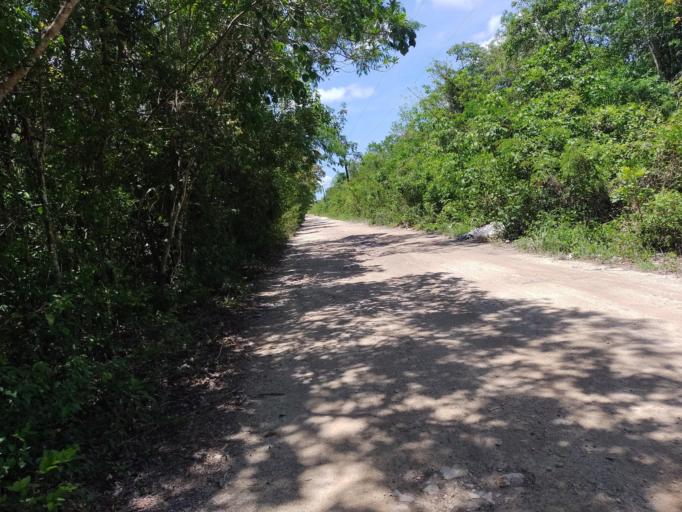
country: MX
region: Quintana Roo
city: San Miguel de Cozumel
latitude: 20.4910
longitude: -86.9070
